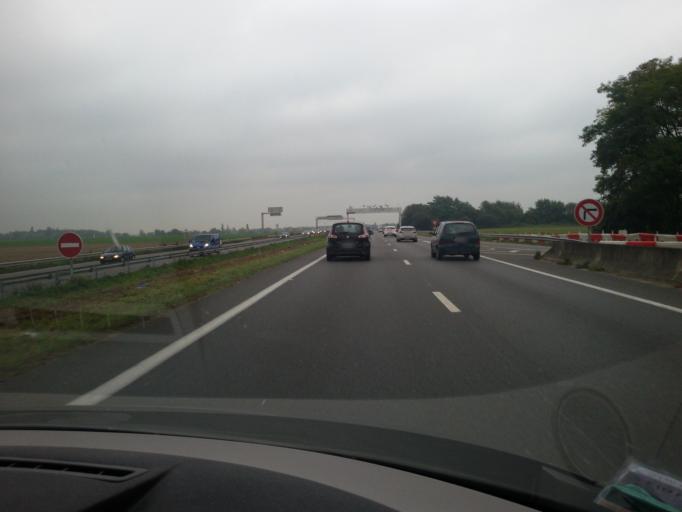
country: FR
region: Ile-de-France
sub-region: Departement de l'Essonne
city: Saclay
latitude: 48.7223
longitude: 2.1680
